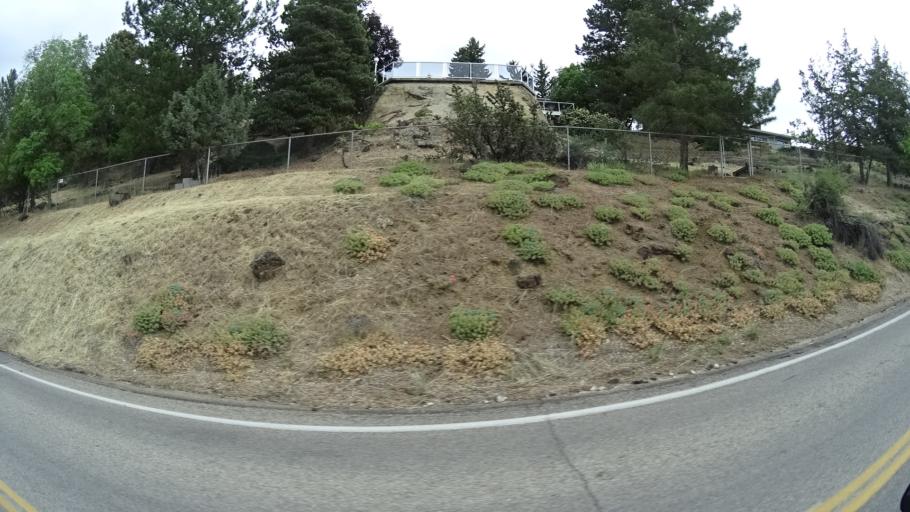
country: US
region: Idaho
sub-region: Ada County
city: Boise
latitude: 43.6137
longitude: -116.1806
